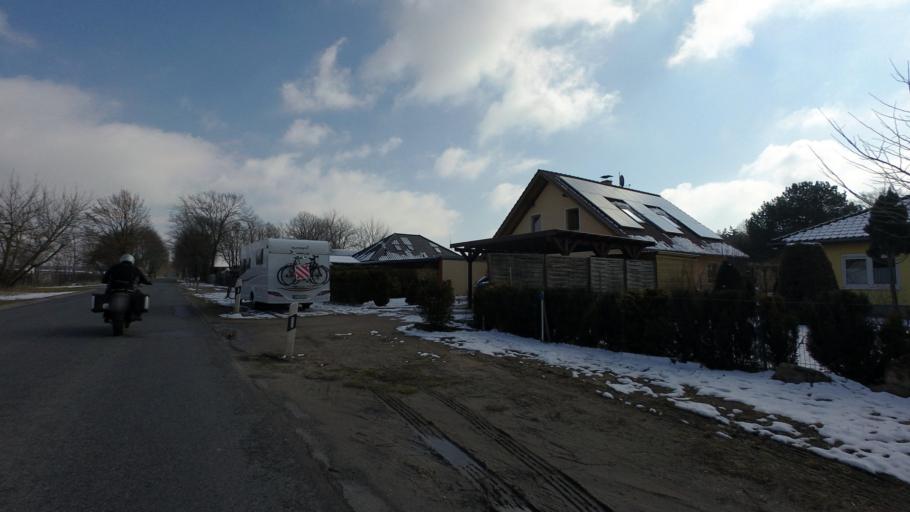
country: DE
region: Brandenburg
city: Bernau bei Berlin
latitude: 52.6869
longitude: 13.6075
